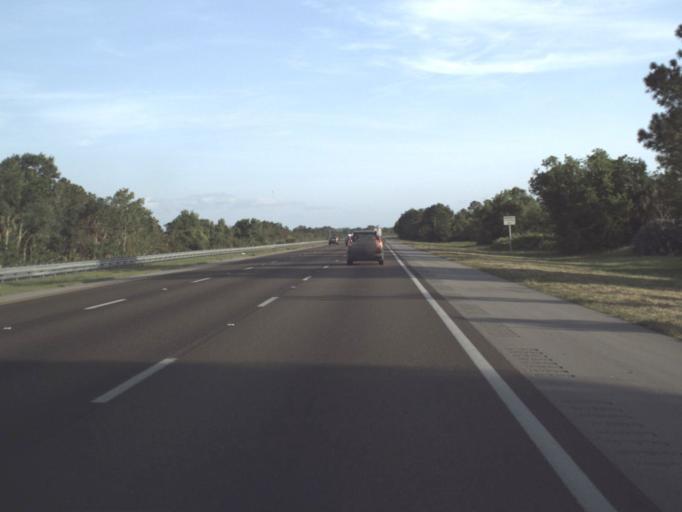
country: US
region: Florida
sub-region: Brevard County
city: Mims
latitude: 28.7498
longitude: -80.8880
